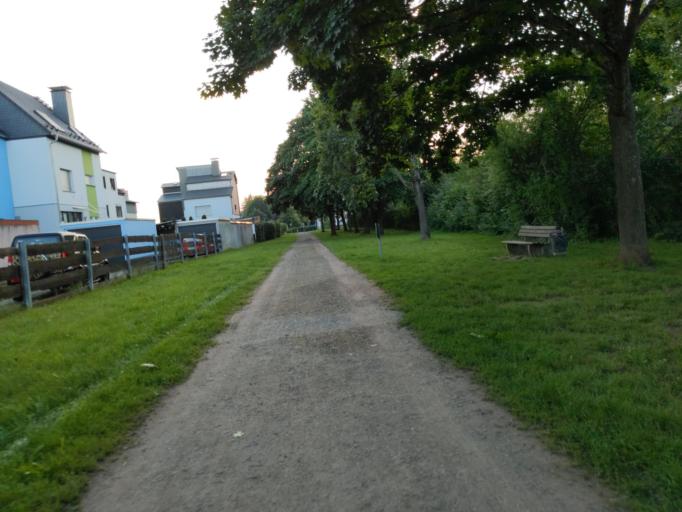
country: DE
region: Hesse
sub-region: Regierungsbezirk Darmstadt
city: Rodgau
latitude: 50.0534
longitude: 8.8977
